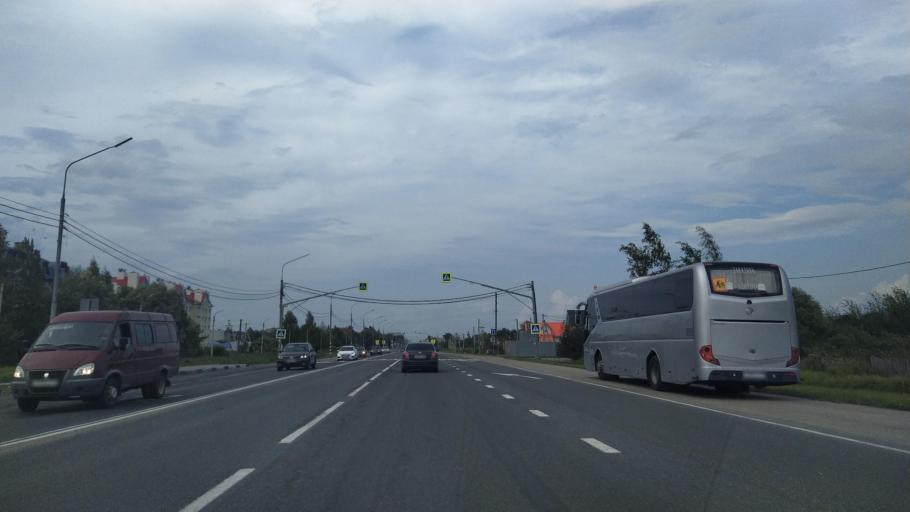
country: RU
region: Novgorod
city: Pankovka
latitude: 58.4929
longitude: 31.2065
